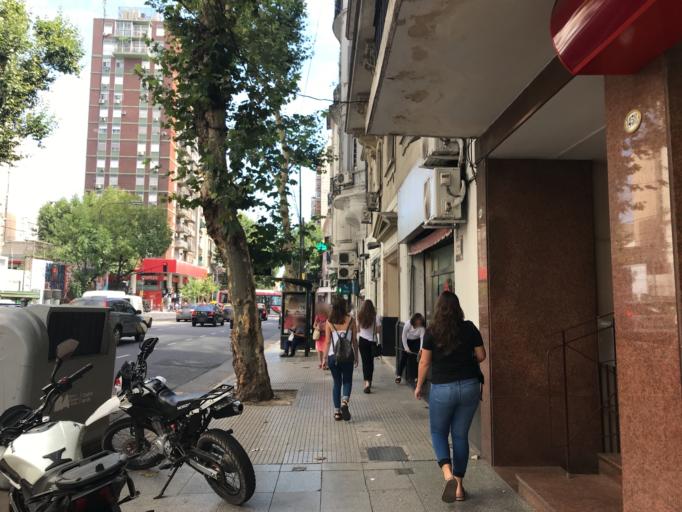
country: AR
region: Buenos Aires F.D.
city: Retiro
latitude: -34.5938
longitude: -58.4021
